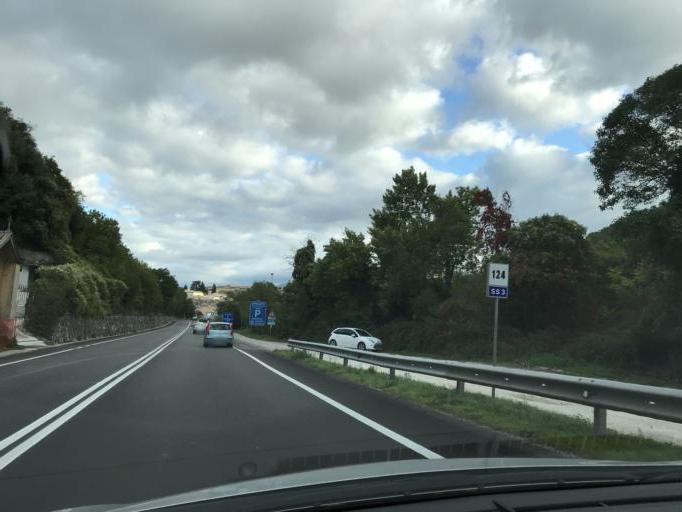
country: IT
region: Umbria
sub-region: Provincia di Perugia
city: Spoleto
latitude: 42.7244
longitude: 12.7346
